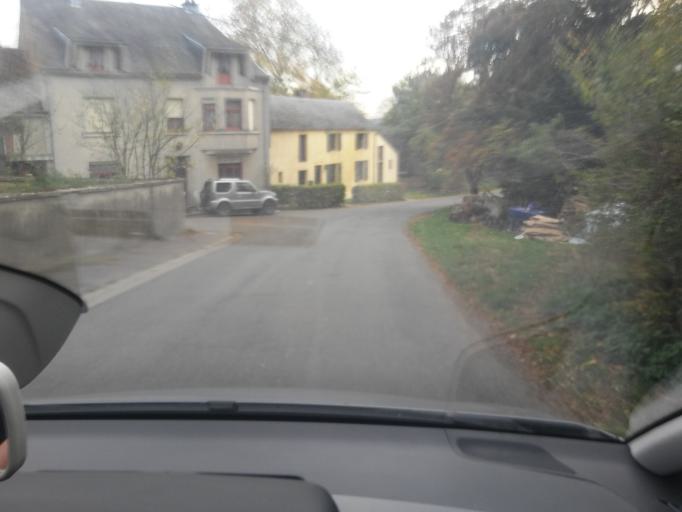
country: BE
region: Wallonia
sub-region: Province du Luxembourg
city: Attert
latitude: 49.7630
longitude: 5.7677
